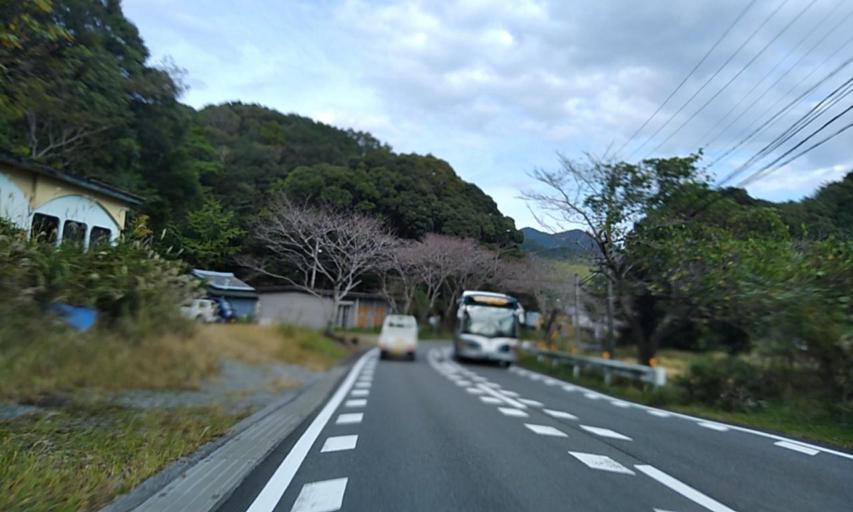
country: JP
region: Mie
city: Ise
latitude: 34.2937
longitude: 136.5783
